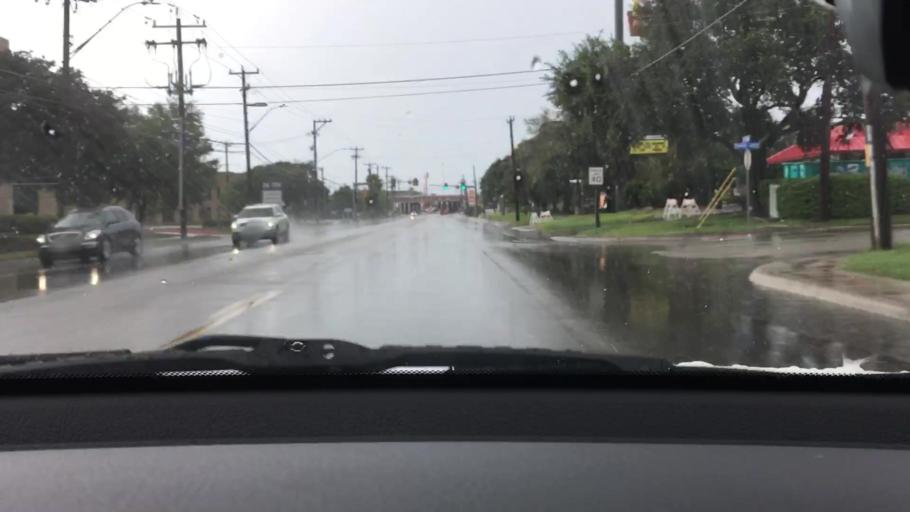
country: US
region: Texas
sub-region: Bexar County
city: Alamo Heights
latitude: 29.5200
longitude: -98.4615
